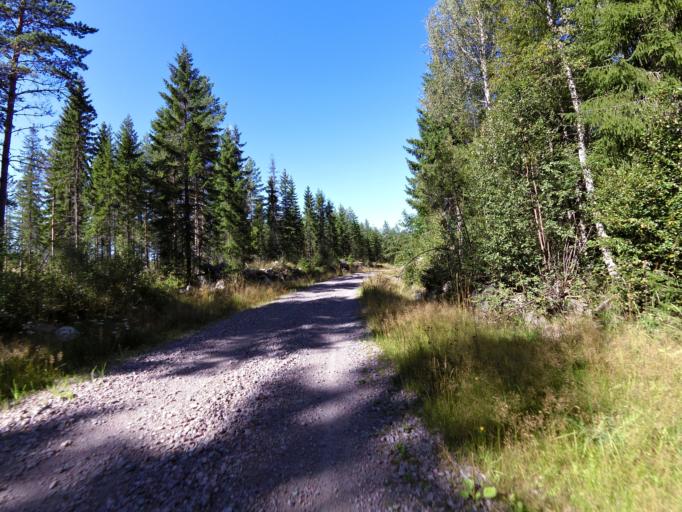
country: SE
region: Gaevleborg
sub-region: Gavle Kommun
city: Valbo
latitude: 60.7305
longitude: 16.9905
